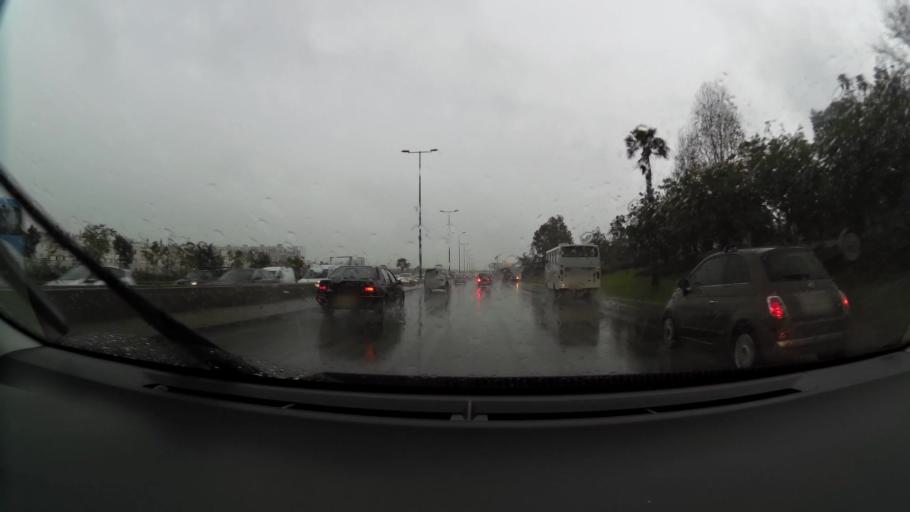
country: MA
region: Grand Casablanca
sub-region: Casablanca
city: Casablanca
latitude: 33.5757
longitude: -7.5609
